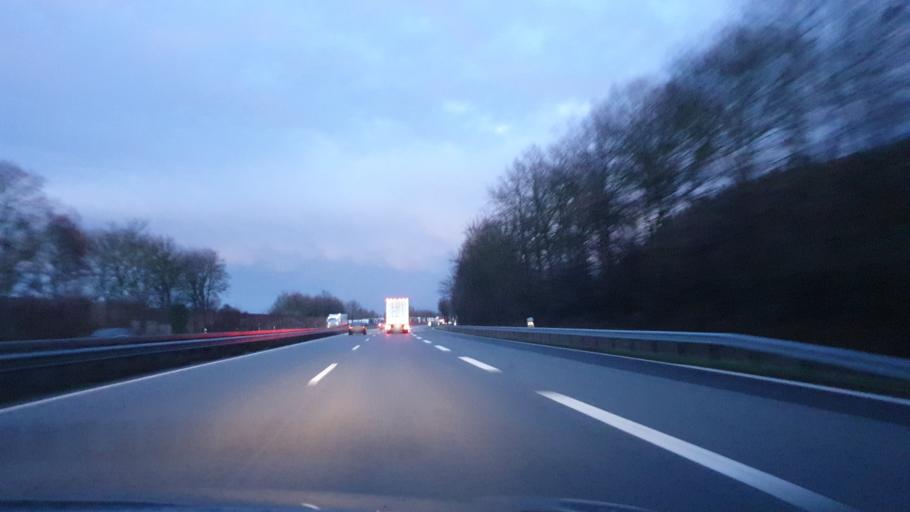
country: DE
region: Rheinland-Pfalz
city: Kretz
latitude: 50.3909
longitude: 7.3627
